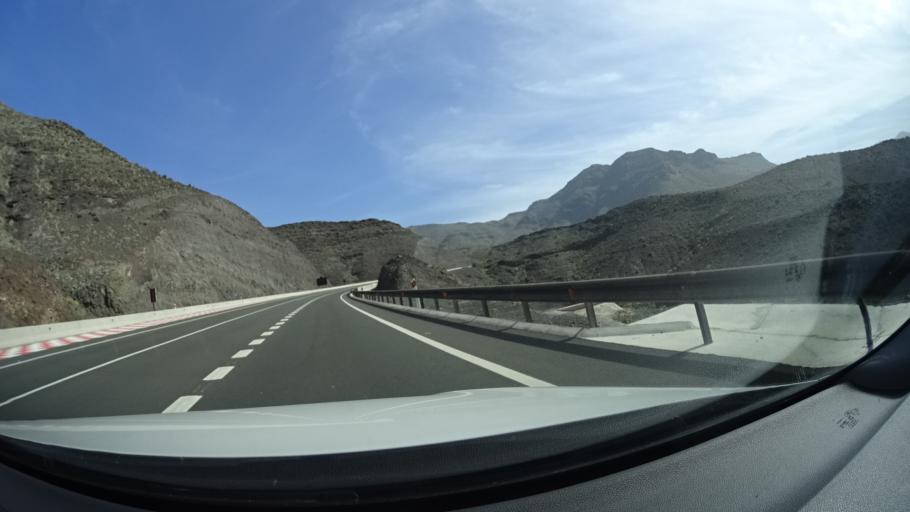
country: ES
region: Canary Islands
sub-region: Provincia de Las Palmas
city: San Nicolas
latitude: 28.0108
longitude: -15.7832
